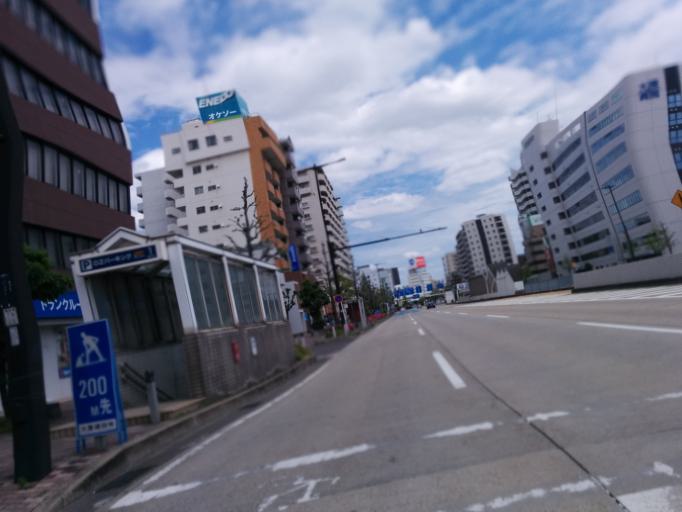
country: JP
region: Aichi
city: Nagoya-shi
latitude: 35.1906
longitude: 136.9312
